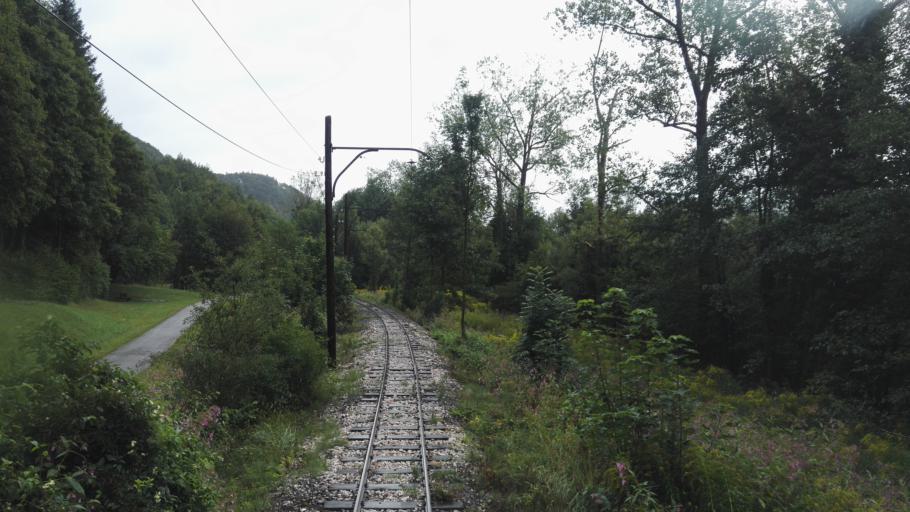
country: AT
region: Lower Austria
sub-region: Politischer Bezirk Neunkirchen
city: Reichenau an der Rax
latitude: 47.7037
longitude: 15.8274
